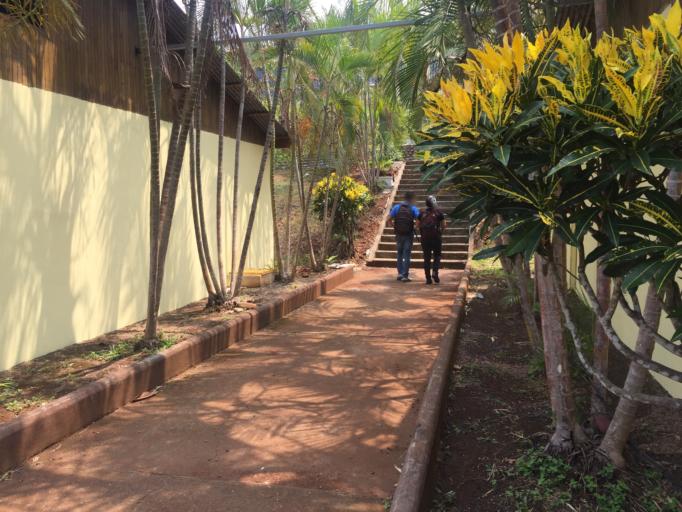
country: CR
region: Puntarenas
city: Esparza
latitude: 9.9978
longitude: -84.6757
